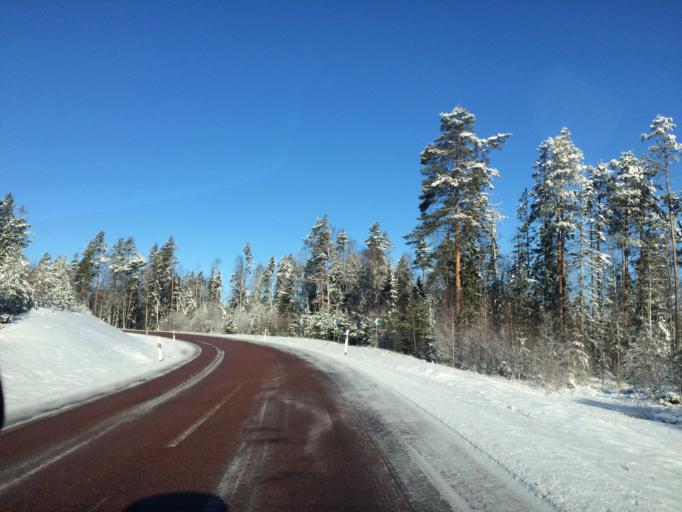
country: SE
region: Dalarna
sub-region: Mora Kommun
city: Mora
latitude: 60.8528
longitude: 14.2547
